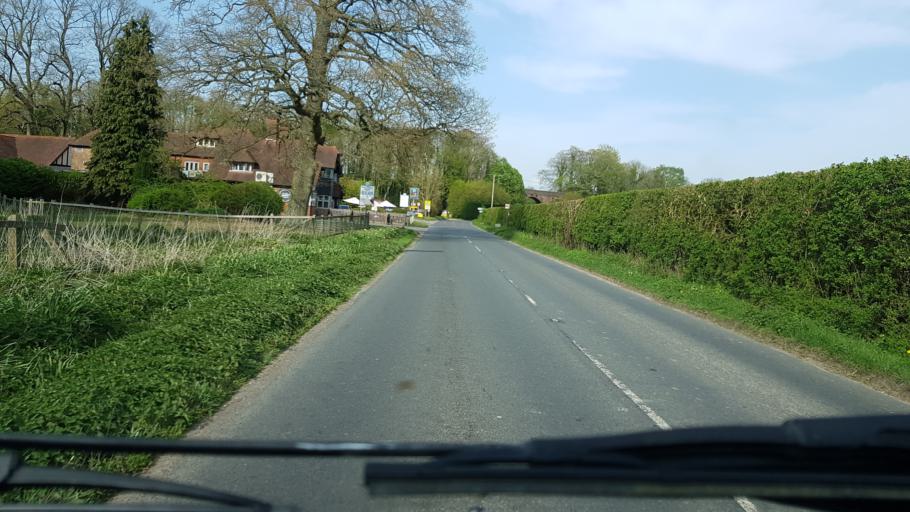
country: GB
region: England
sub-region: Hampshire
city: Overton
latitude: 51.2537
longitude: -1.1933
